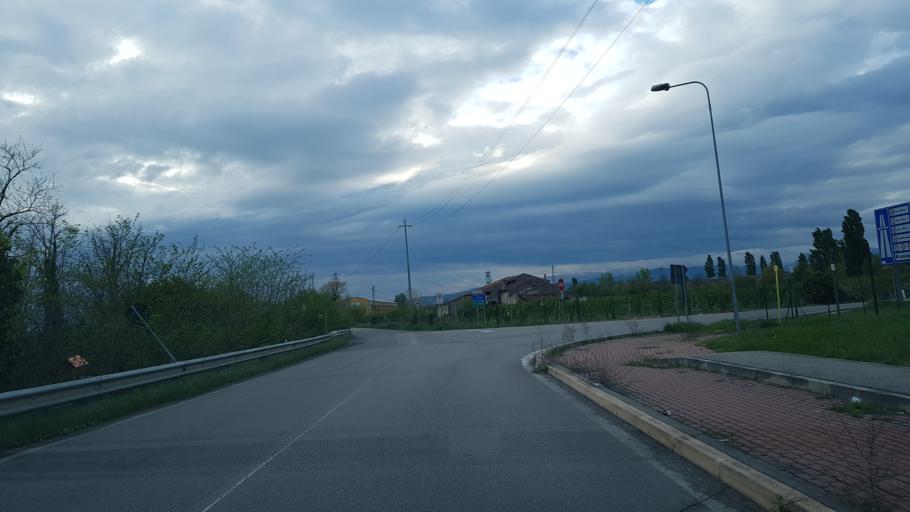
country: IT
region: Veneto
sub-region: Provincia di Verona
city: San Martino Buon Albergo
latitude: 45.4201
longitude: 11.0749
